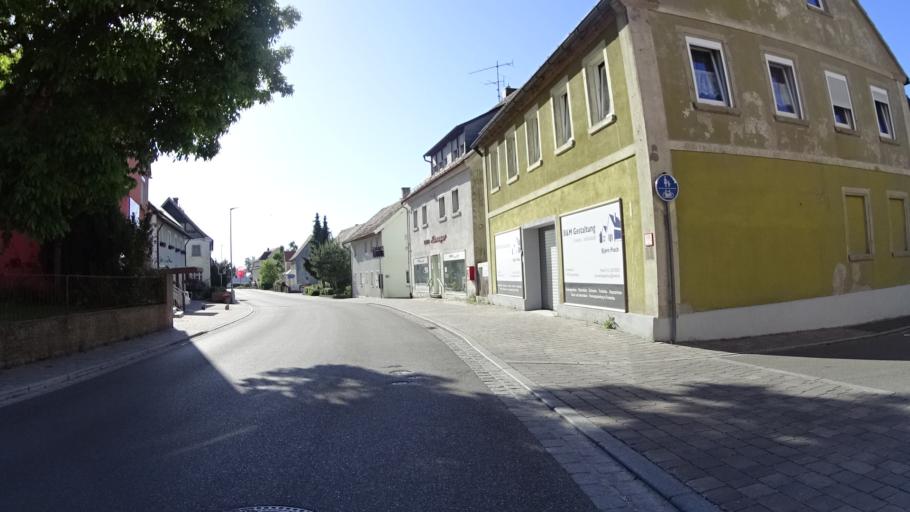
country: DE
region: Bavaria
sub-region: Regierungsbezirk Mittelfranken
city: Arberg
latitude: 49.1582
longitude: 10.5514
